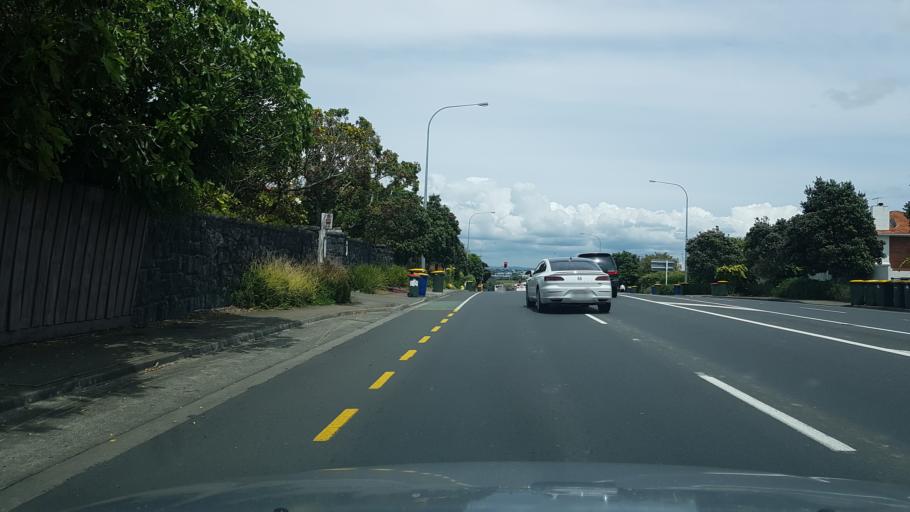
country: NZ
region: Auckland
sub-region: Auckland
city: North Shore
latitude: -36.7937
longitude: 174.7749
